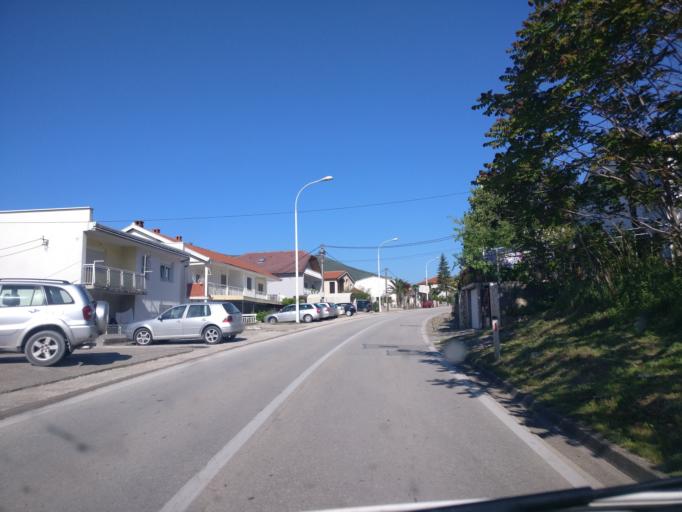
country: BA
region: Federation of Bosnia and Herzegovina
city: Capljina
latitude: 43.1194
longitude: 17.6891
